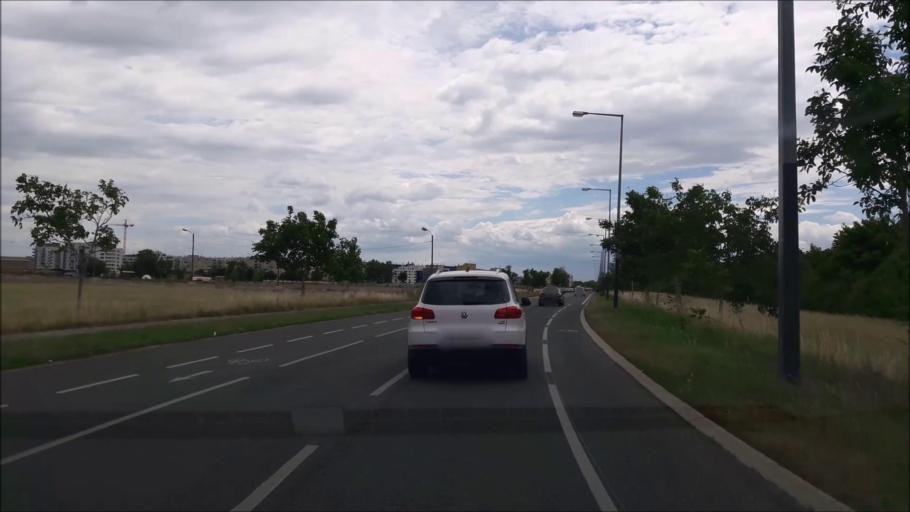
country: AT
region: Lower Austria
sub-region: Politischer Bezirk Ganserndorf
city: Gross-Enzersdorf
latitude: 48.2334
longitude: 16.4999
